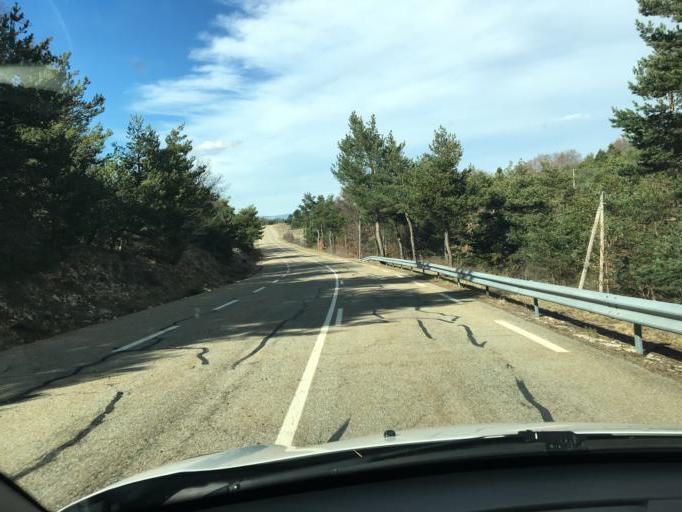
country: FR
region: Provence-Alpes-Cote d'Azur
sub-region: Departement du Vaucluse
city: Saint-Saturnin-les-Apt
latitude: 43.9894
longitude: 5.4762
